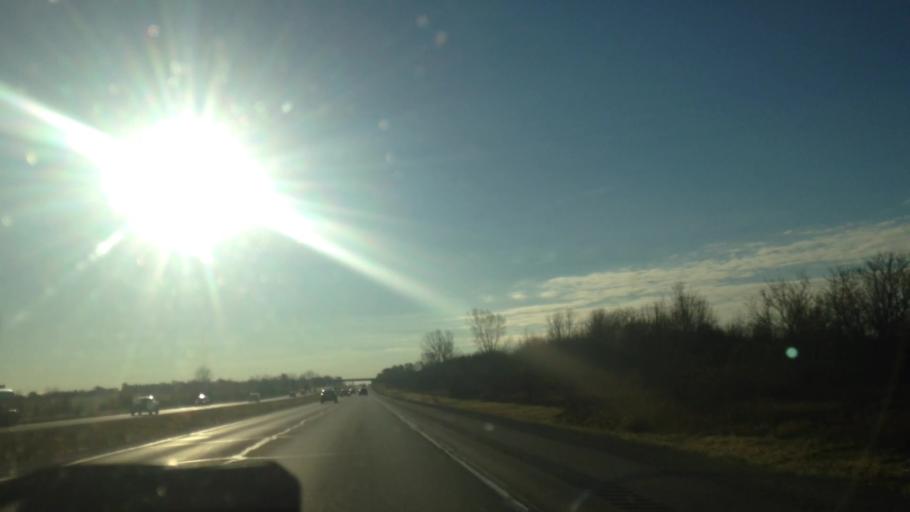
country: US
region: Wisconsin
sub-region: Washington County
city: Richfield
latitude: 43.3025
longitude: -88.2208
